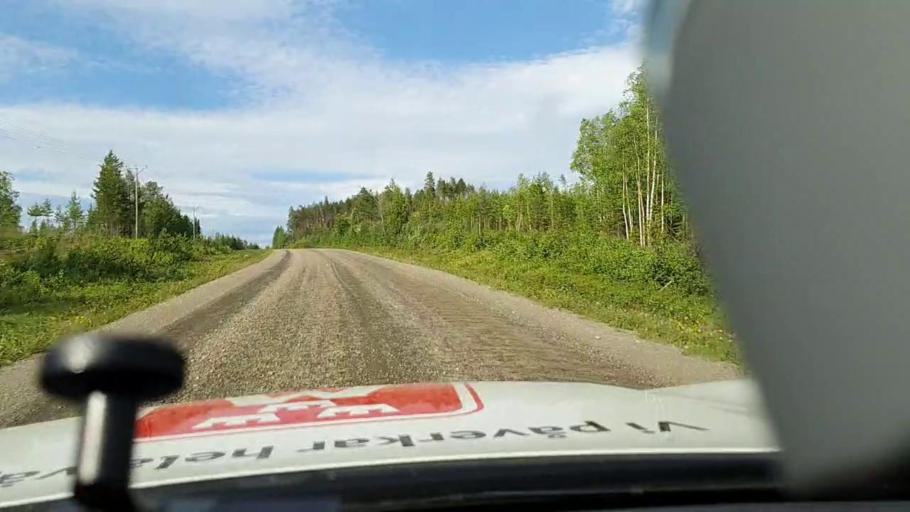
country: SE
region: Norrbotten
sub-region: Alvsbyns Kommun
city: AElvsbyn
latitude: 66.1662
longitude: 21.0571
